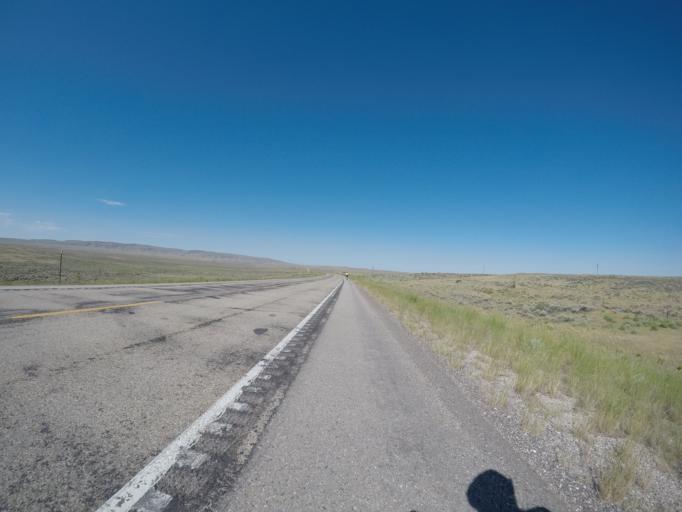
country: US
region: Wyoming
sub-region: Carbon County
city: Saratoga
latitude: 41.8256
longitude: -106.6410
